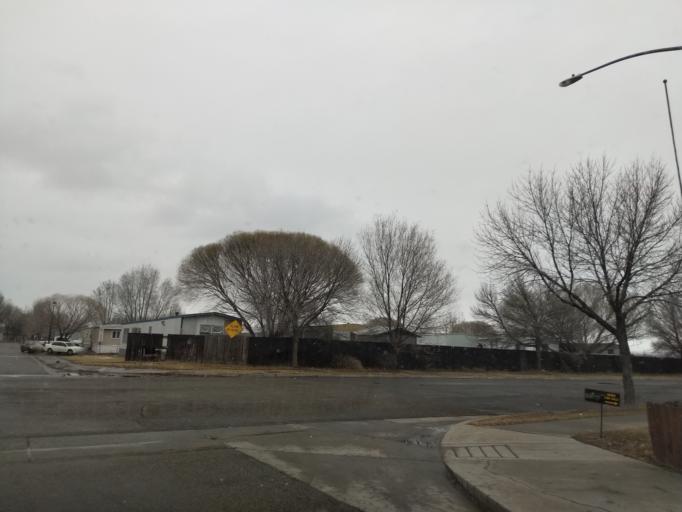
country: US
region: Colorado
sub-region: Mesa County
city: Grand Junction
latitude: 39.0747
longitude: -108.5293
